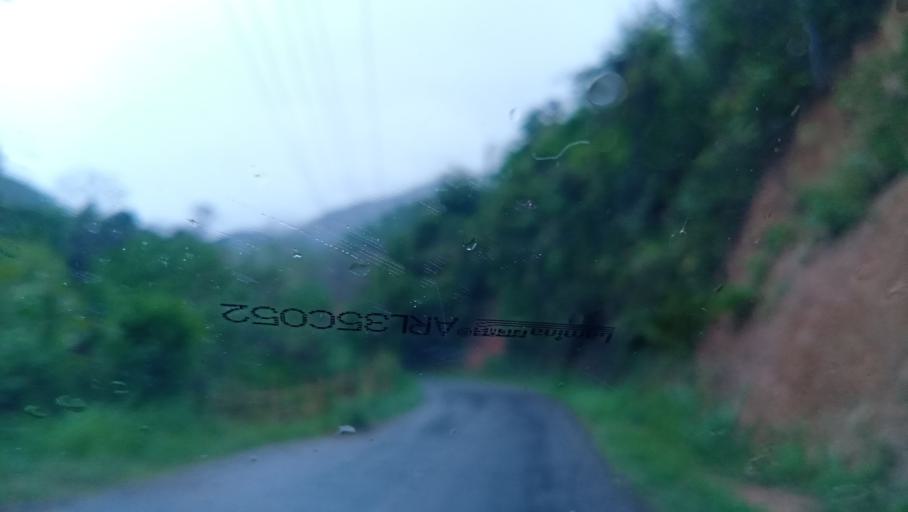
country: LA
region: Phongsali
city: Khoa
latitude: 21.0629
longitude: 102.4839
